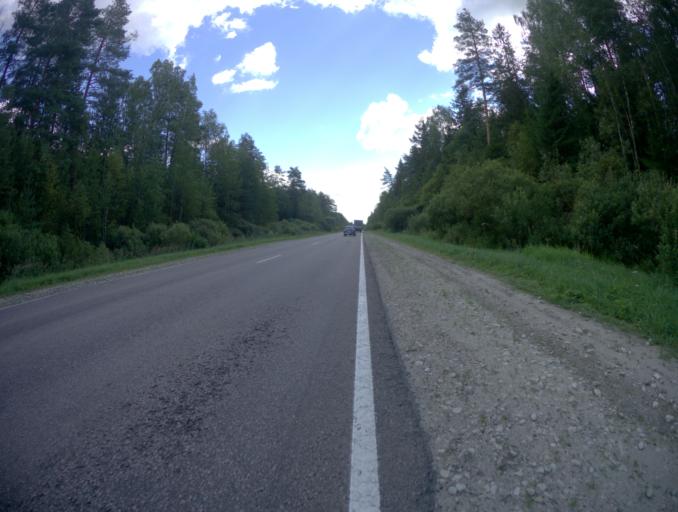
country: RU
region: Vladimir
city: Orgtrud
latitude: 56.0019
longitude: 40.6552
